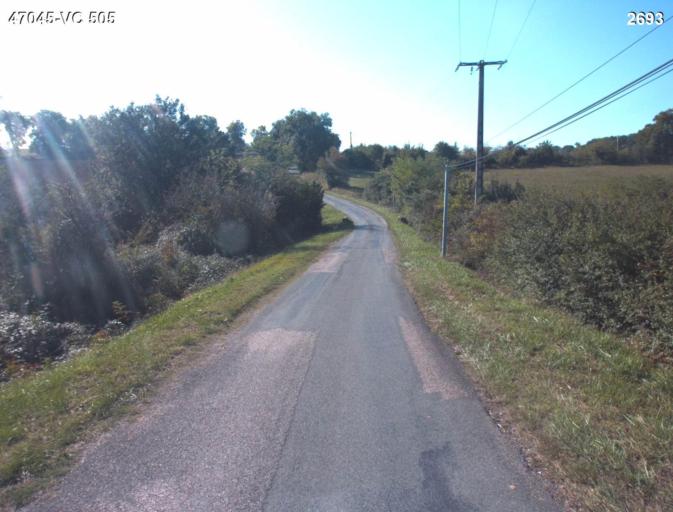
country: FR
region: Aquitaine
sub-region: Departement du Lot-et-Garonne
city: Nerac
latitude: 44.1408
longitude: 0.4164
